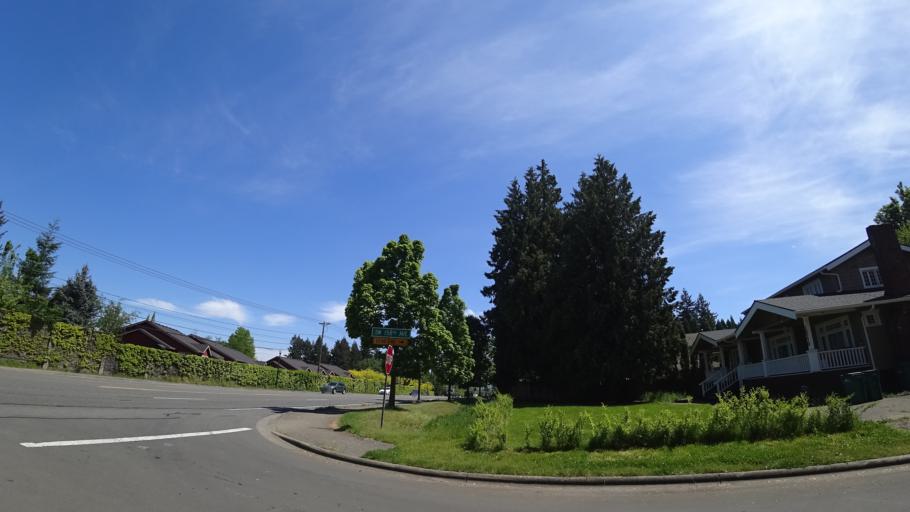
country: US
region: Oregon
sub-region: Washington County
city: Aloha
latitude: 45.4840
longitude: -122.8396
